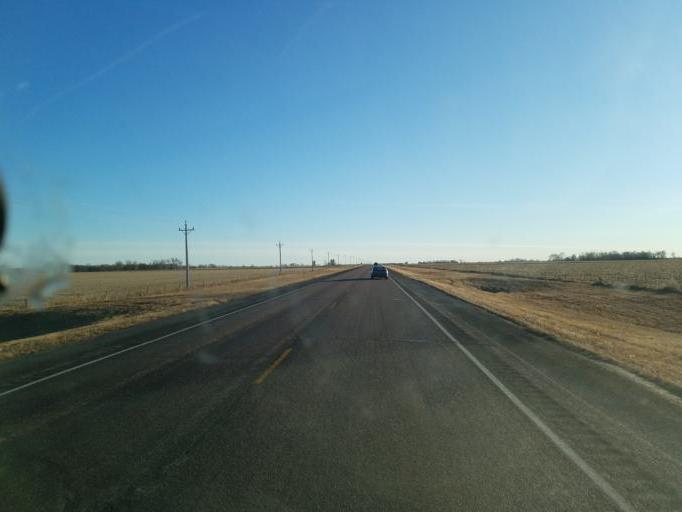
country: US
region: South Dakota
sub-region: Hutchinson County
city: Parkston
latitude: 43.1943
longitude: -97.9719
